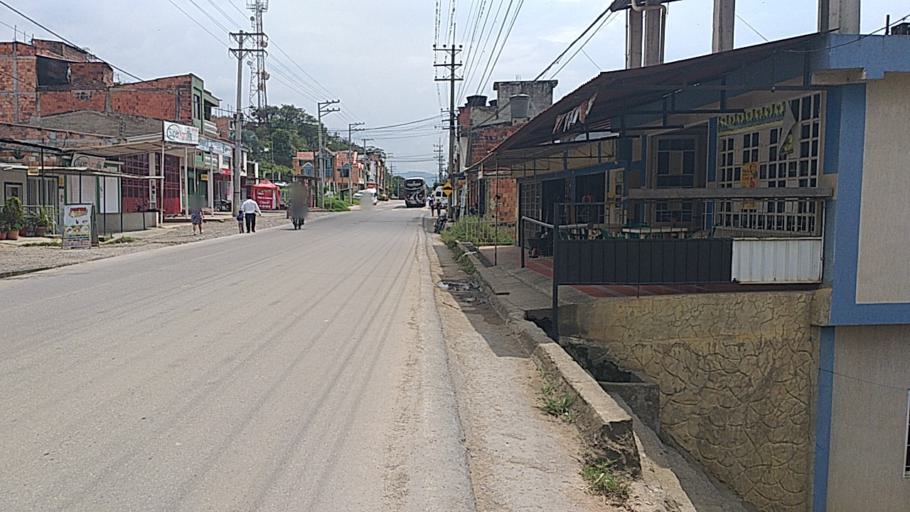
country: CO
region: Boyaca
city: Santana
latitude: 6.0567
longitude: -73.4804
